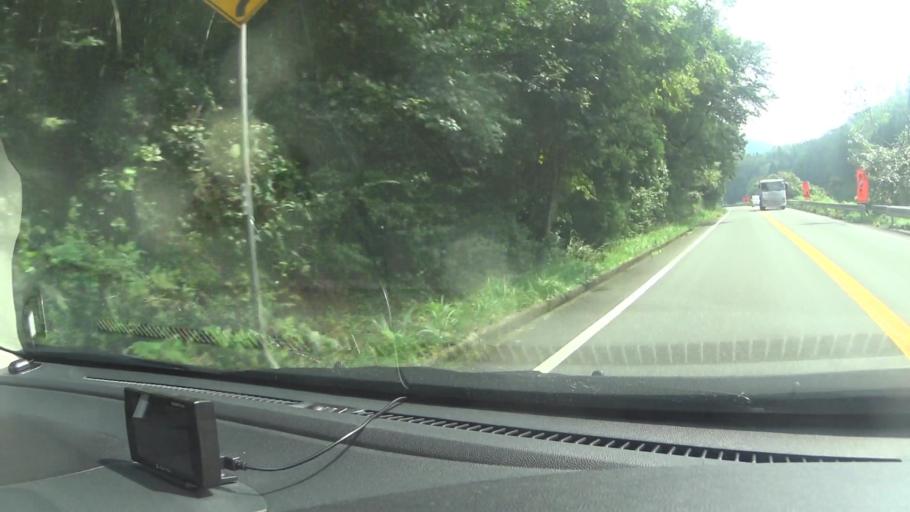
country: JP
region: Hyogo
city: Sasayama
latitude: 35.1437
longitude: 135.3465
